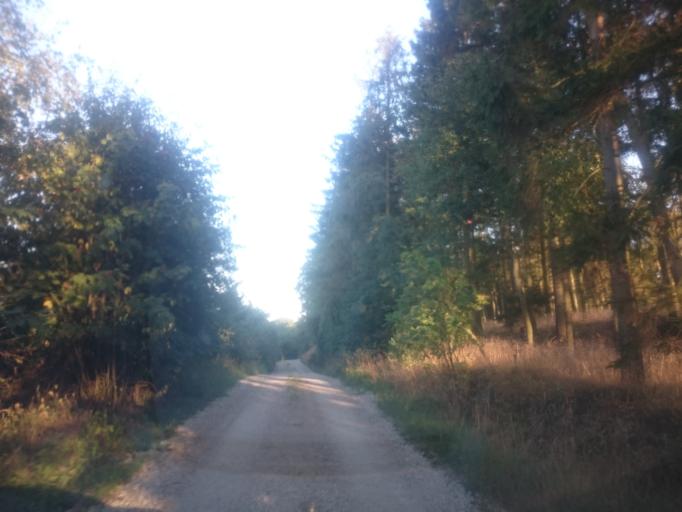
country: DK
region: South Denmark
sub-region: Billund Kommune
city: Billund
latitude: 55.7299
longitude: 9.0403
